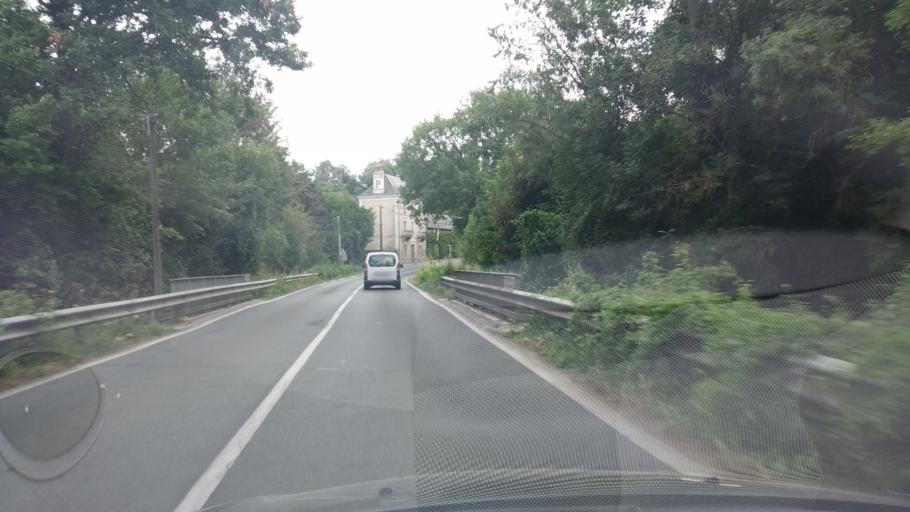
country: FR
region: Poitou-Charentes
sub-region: Departement de la Vienne
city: Saint-Benoit
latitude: 46.5537
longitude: 0.3513
